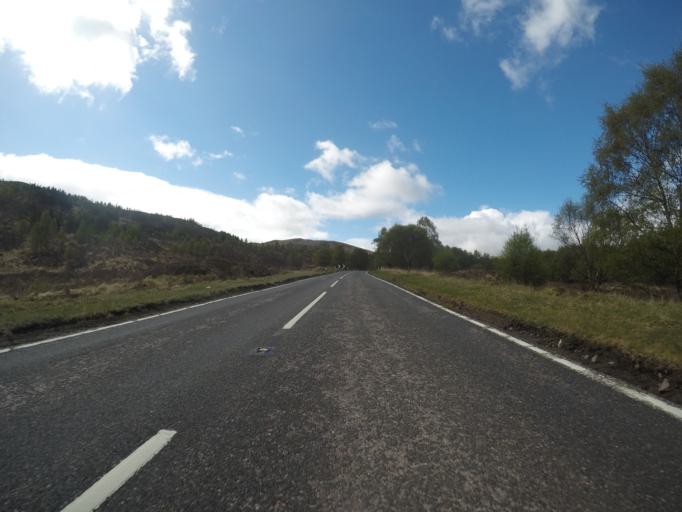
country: GB
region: Scotland
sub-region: Highland
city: Spean Bridge
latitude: 57.1270
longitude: -4.9650
